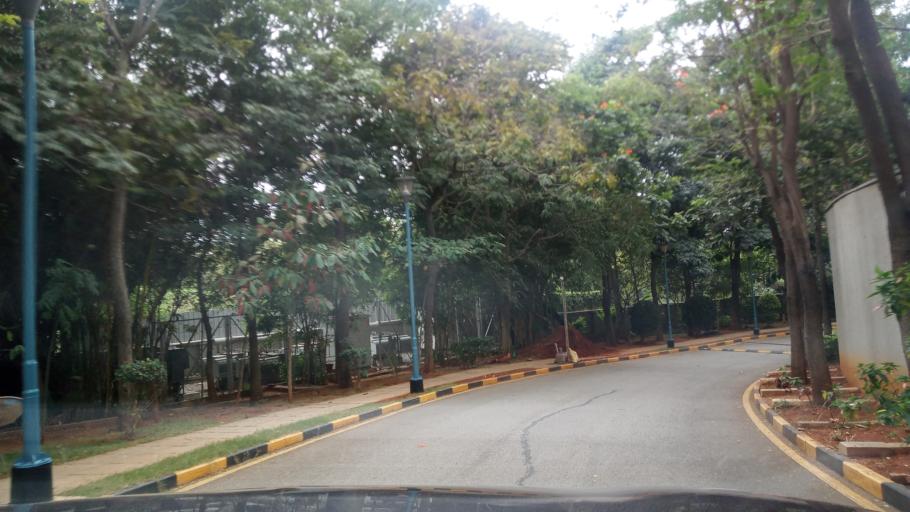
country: IN
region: Karnataka
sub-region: Bangalore Urban
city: Yelahanka
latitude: 13.0445
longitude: 77.5011
